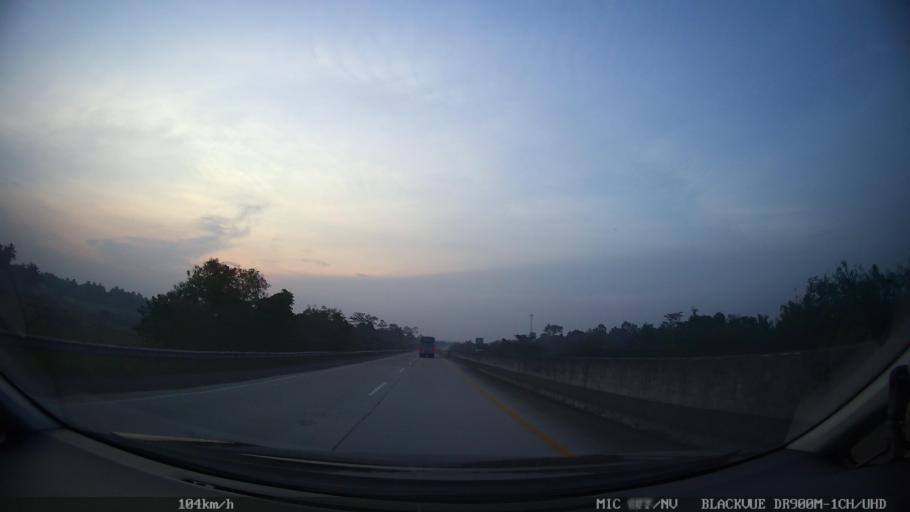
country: ID
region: Lampung
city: Pasuruan
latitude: -5.7129
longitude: 105.6506
